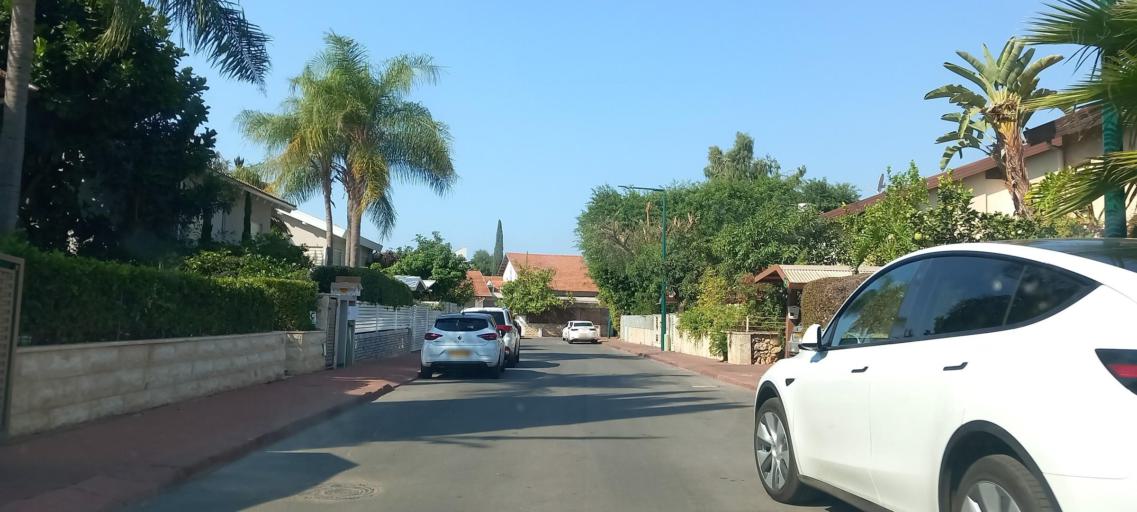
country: IL
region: Tel Aviv
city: Or Yehuda
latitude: 32.0438
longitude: 34.8361
